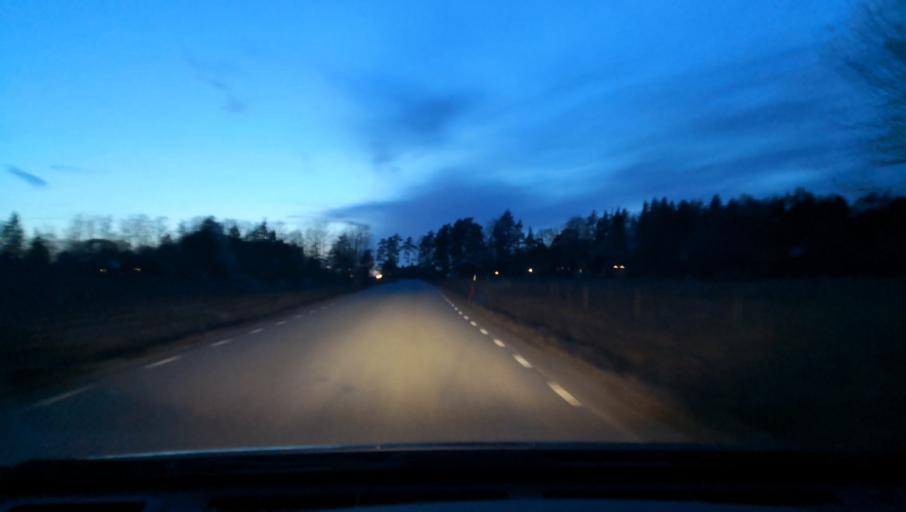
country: SE
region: Uppsala
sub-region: Enkopings Kommun
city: Grillby
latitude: 59.6065
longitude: 17.2864
